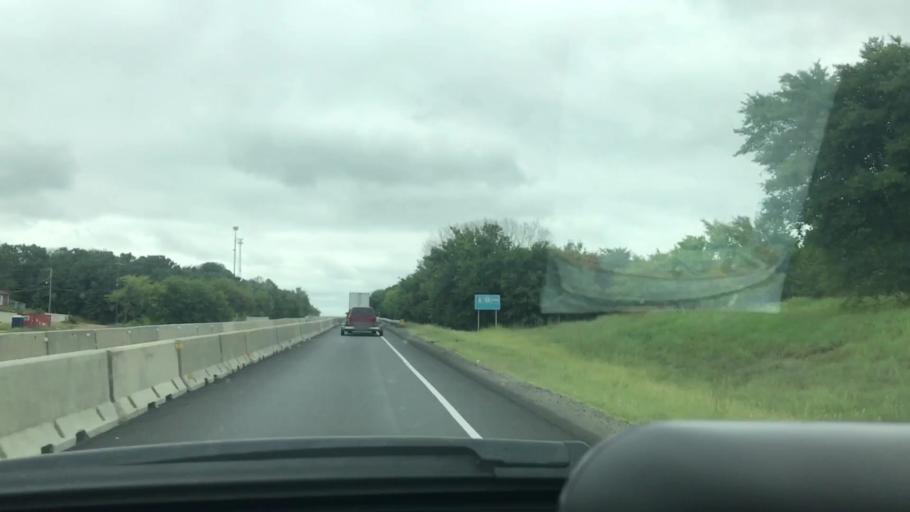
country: US
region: Oklahoma
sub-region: McIntosh County
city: Eufaula
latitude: 35.2829
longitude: -95.5931
